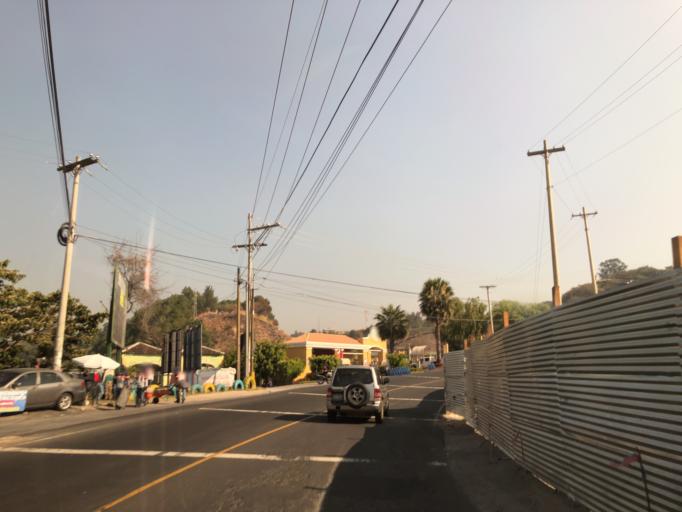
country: GT
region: Guatemala
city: Petapa
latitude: 14.5036
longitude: -90.5434
